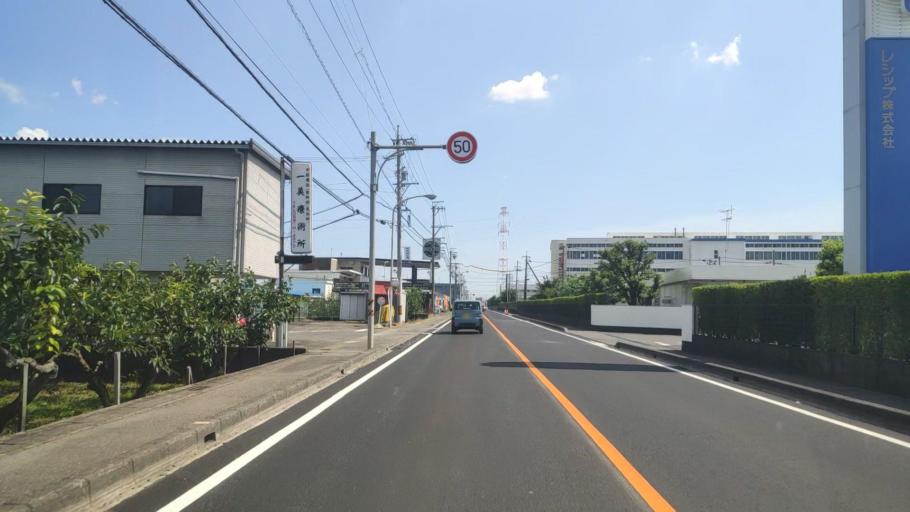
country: JP
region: Gifu
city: Godo
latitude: 35.4659
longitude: 136.6756
